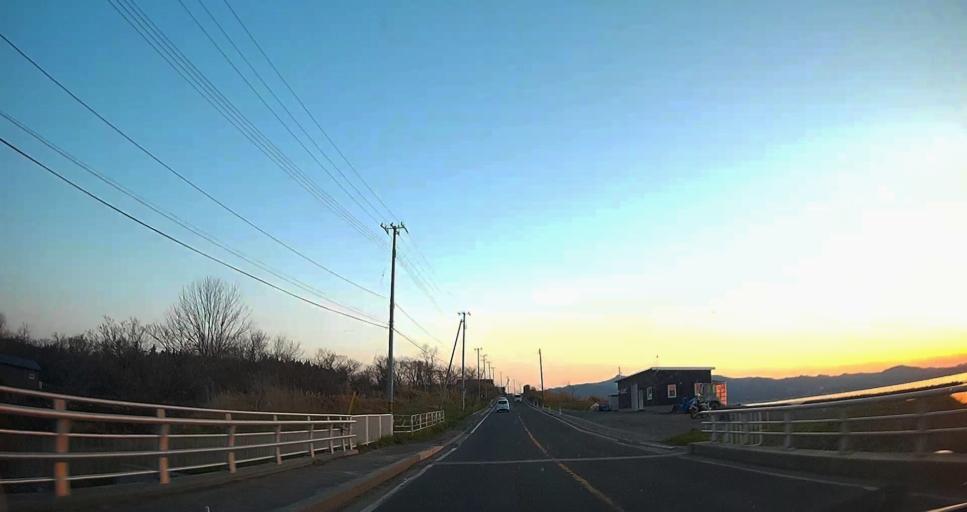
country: JP
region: Aomori
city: Misawa
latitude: 40.8801
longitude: 141.1509
